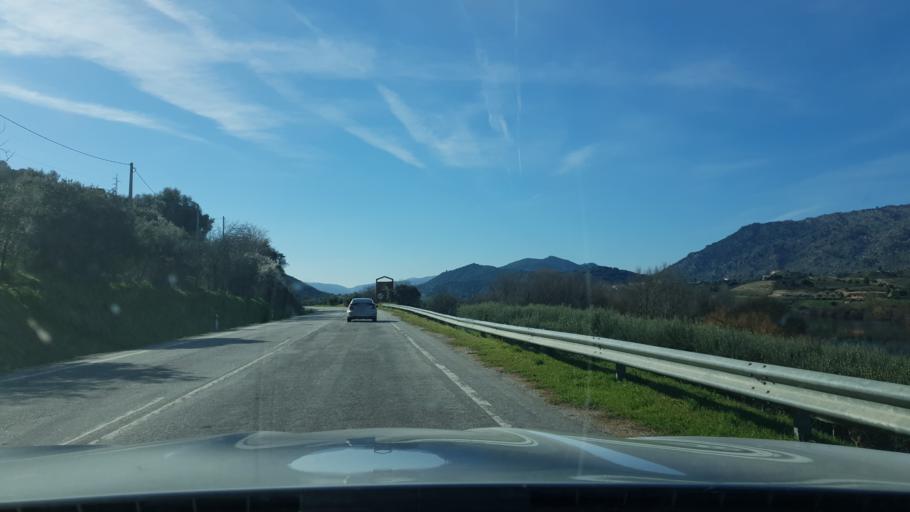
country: PT
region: Braganca
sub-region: Torre de Moncorvo
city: Torre de Moncorvo
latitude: 41.1914
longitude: -7.0990
